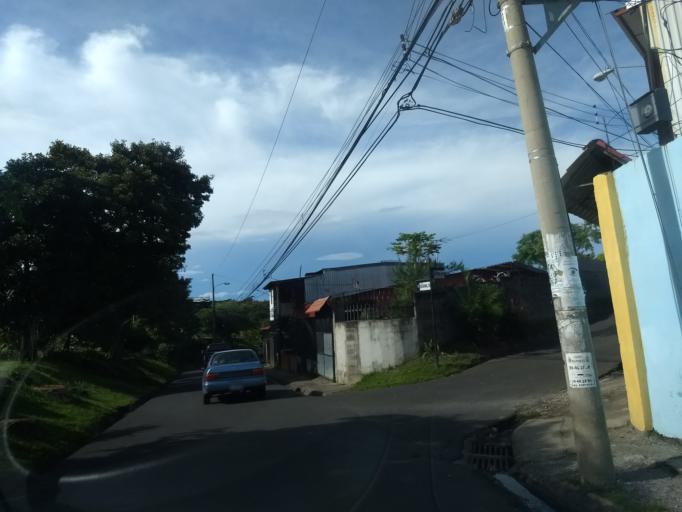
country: CR
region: Heredia
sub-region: Canton de Belen
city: San Antonio
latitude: 9.9761
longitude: -84.1989
